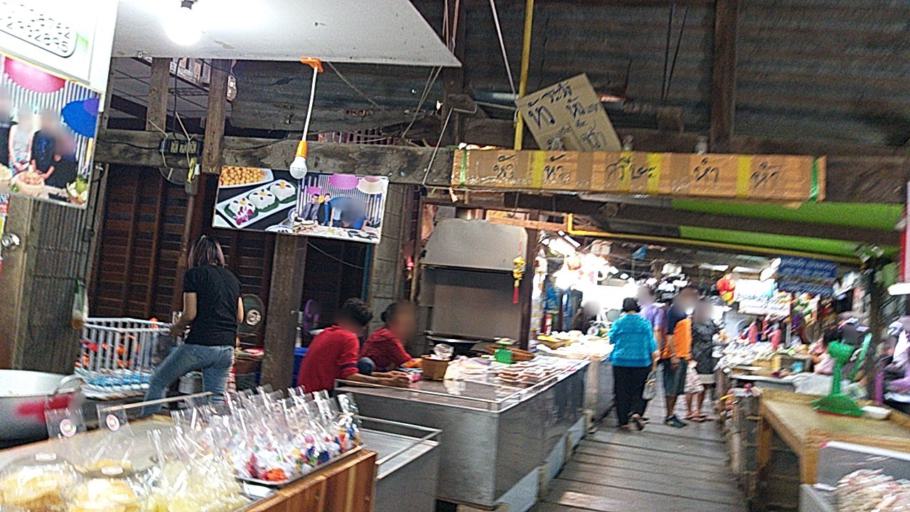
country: TH
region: Nakhon Pathom
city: Salaya
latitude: 13.7690
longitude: 100.2845
